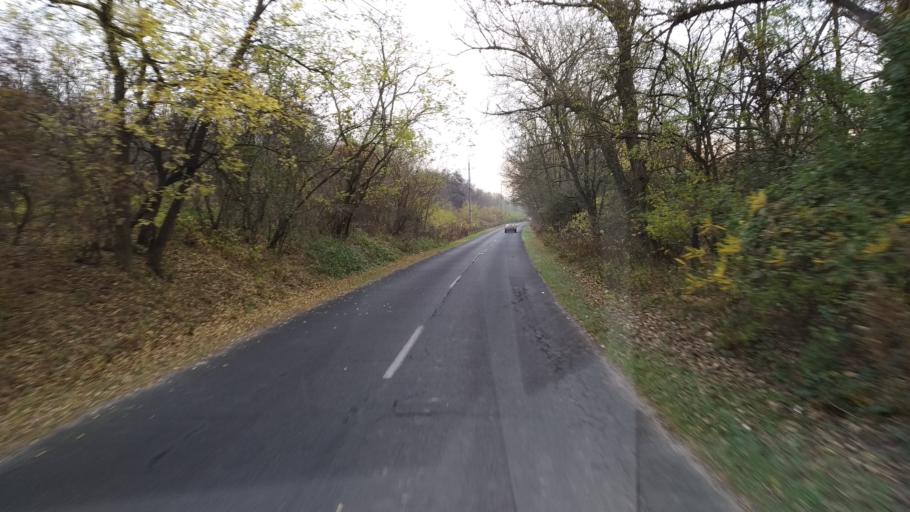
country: HU
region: Pest
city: Dunabogdany
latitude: 47.7948
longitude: 19.0684
